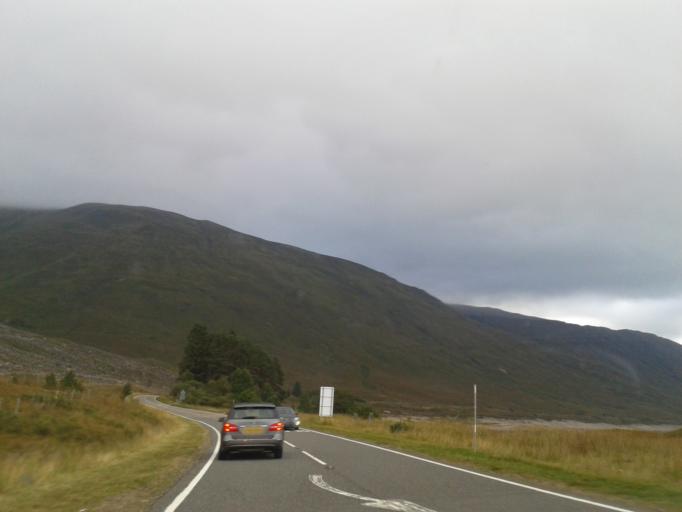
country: GB
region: Scotland
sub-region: Highland
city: Fort William
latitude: 57.1564
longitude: -5.1732
